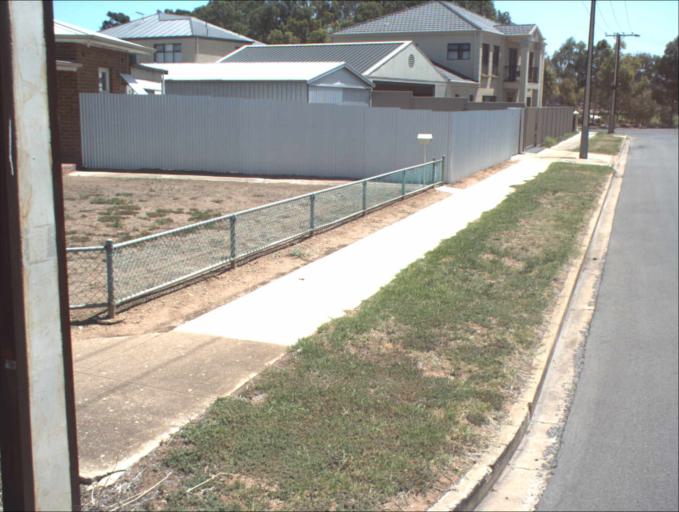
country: AU
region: South Australia
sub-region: Charles Sturt
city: Woodville North
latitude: -34.8606
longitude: 138.5546
